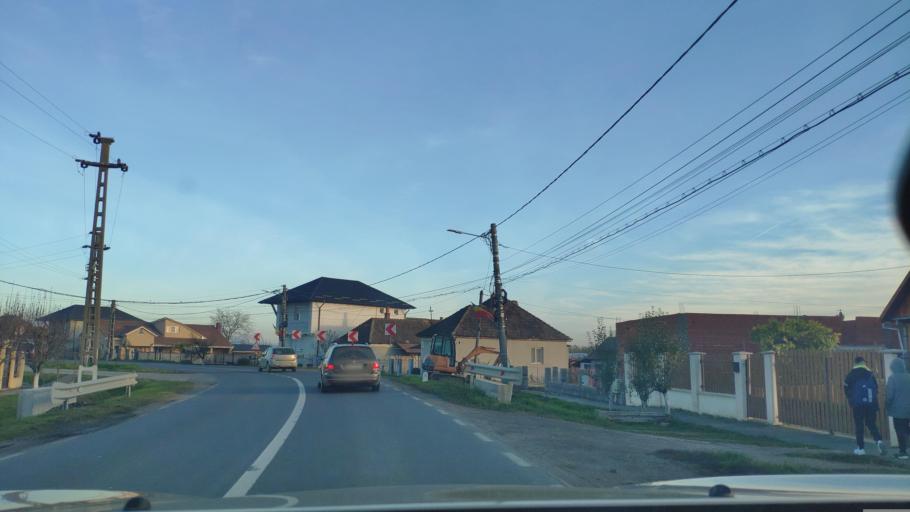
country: RO
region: Satu Mare
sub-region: Comuna Odoreu
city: Odoreu
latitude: 47.7922
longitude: 22.9984
